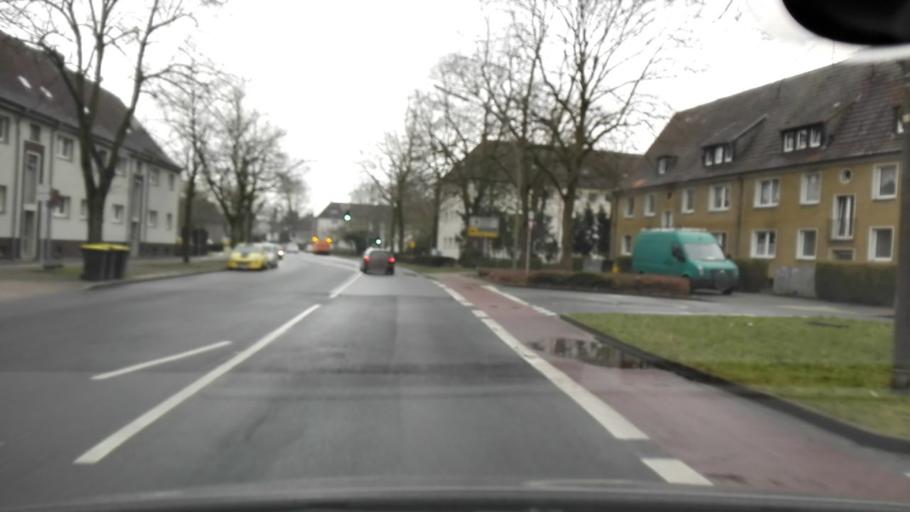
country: DE
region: North Rhine-Westphalia
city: Kamen
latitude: 51.5894
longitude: 7.6580
